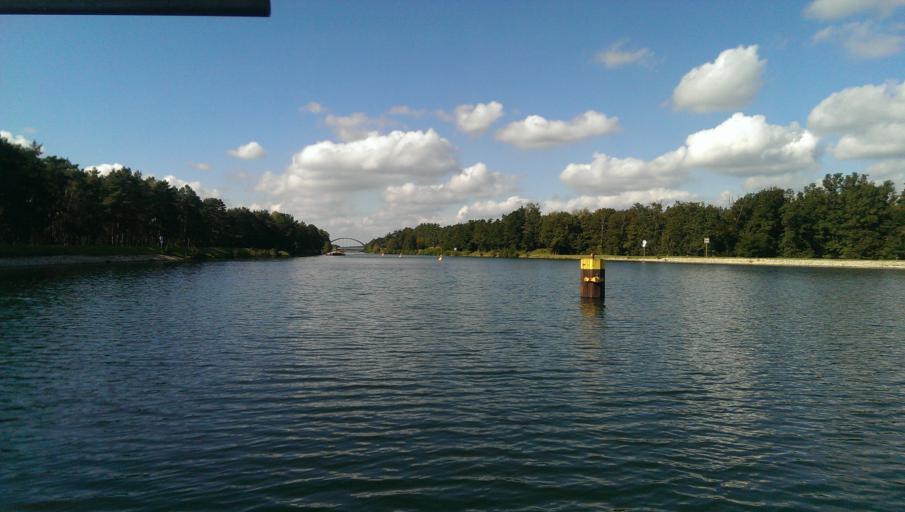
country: DE
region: Brandenburg
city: Niederfinow
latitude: 52.8521
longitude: 13.9221
